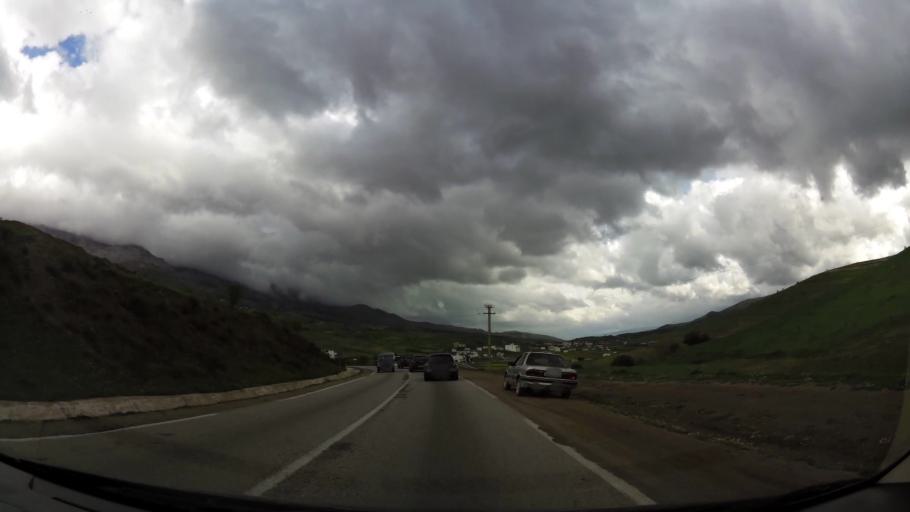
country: MA
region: Tanger-Tetouan
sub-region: Tetouan
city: Zinat
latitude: 35.3381
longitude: -5.3629
